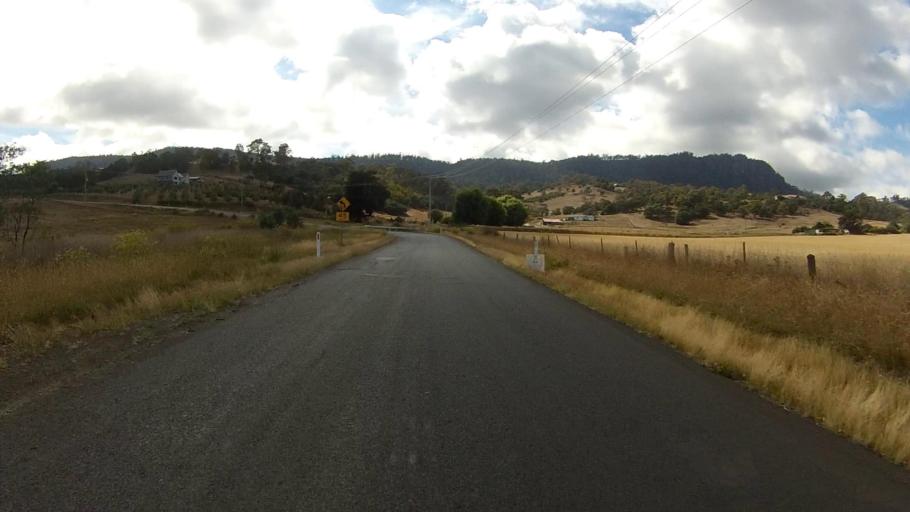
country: AU
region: Tasmania
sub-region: Brighton
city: Old Beach
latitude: -42.7593
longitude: 147.3032
